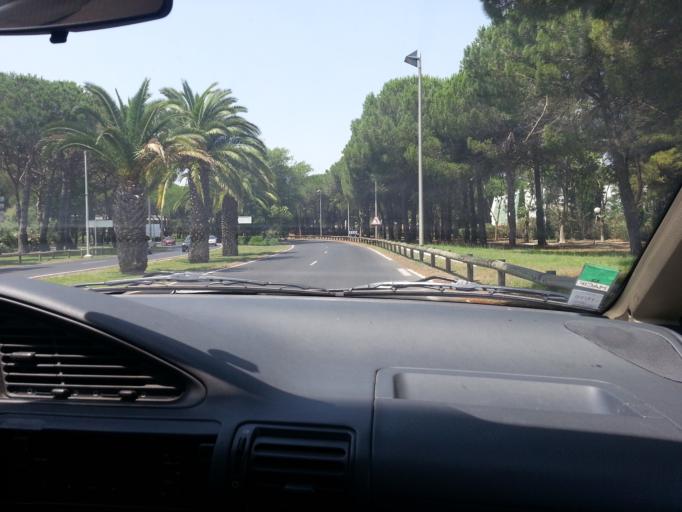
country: FR
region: Languedoc-Roussillon
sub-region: Departement de l'Herault
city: La Grande-Motte
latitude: 43.5622
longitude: 4.0959
